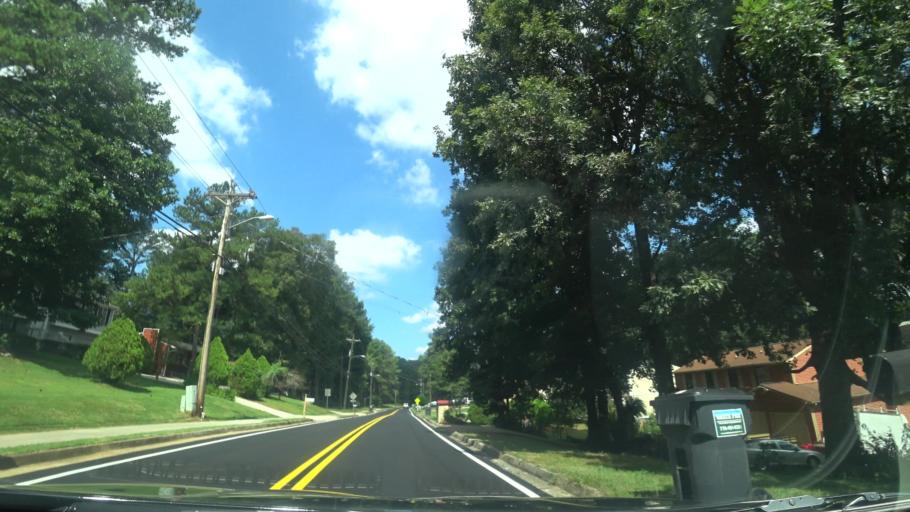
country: US
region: Georgia
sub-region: Gwinnett County
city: Norcross
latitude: 33.9100
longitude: -84.1847
